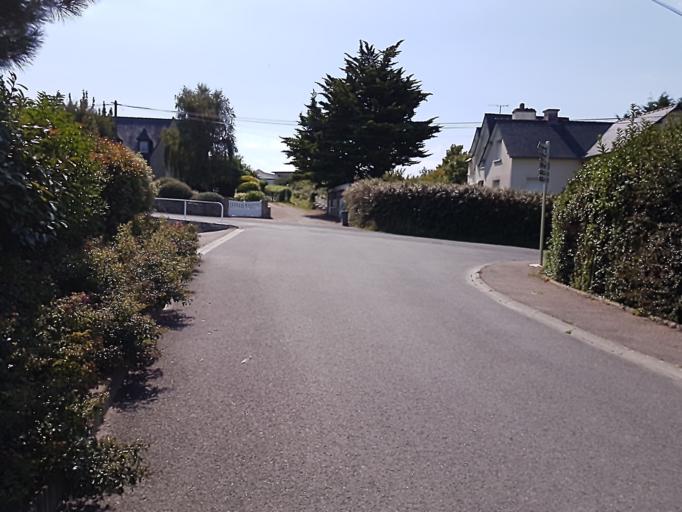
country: FR
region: Brittany
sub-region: Departement des Cotes-d'Armor
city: Saint-Cast-le-Guildo
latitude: 48.6403
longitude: -2.2597
